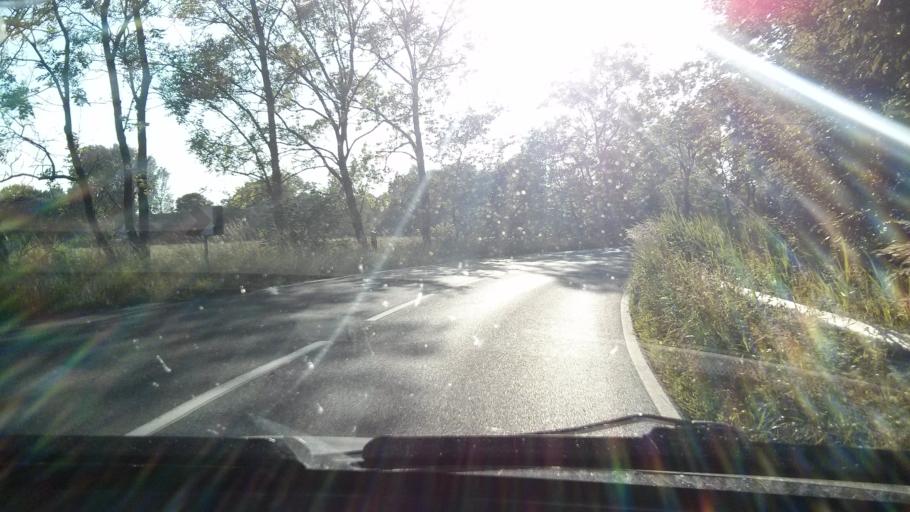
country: DE
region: Lower Saxony
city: Nordenham
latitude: 53.4772
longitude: 8.5557
